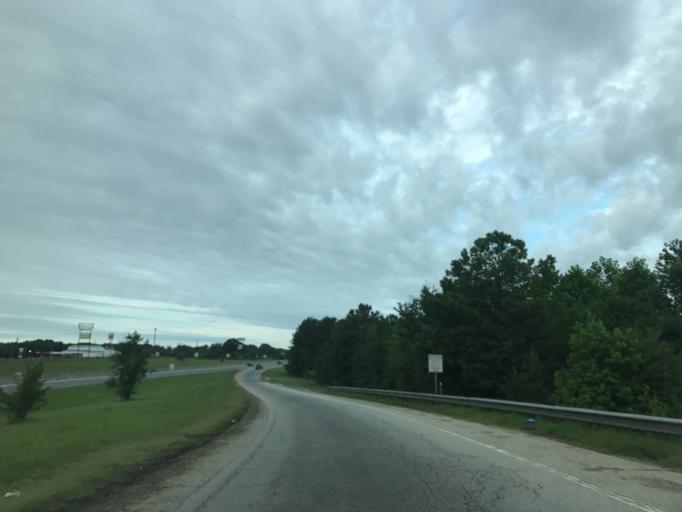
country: US
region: South Carolina
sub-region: Spartanburg County
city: Mayo
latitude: 35.0185
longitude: -81.8972
